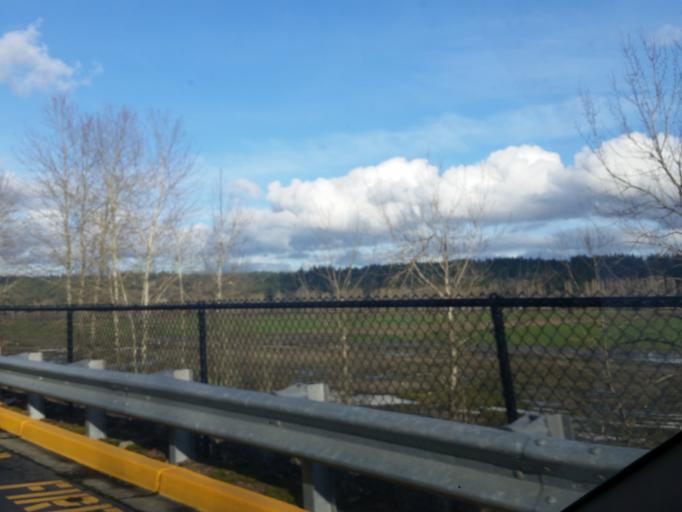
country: US
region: Washington
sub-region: King County
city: Kingsgate
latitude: 47.7167
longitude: -122.1525
